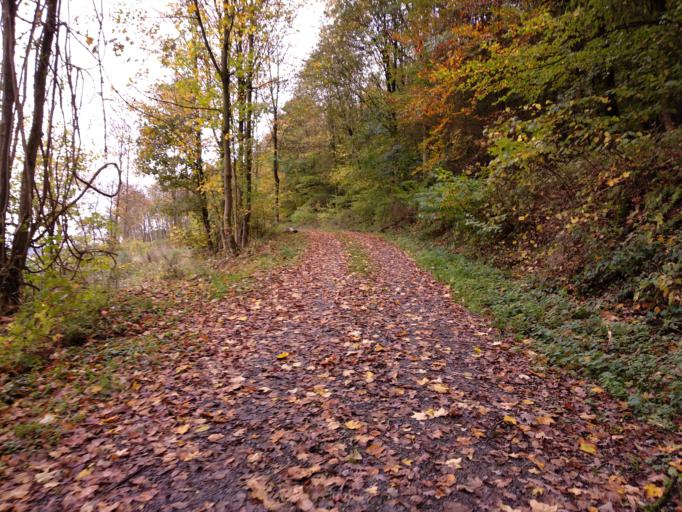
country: DE
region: North Rhine-Westphalia
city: Beverungen
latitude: 51.6707
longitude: 9.3555
